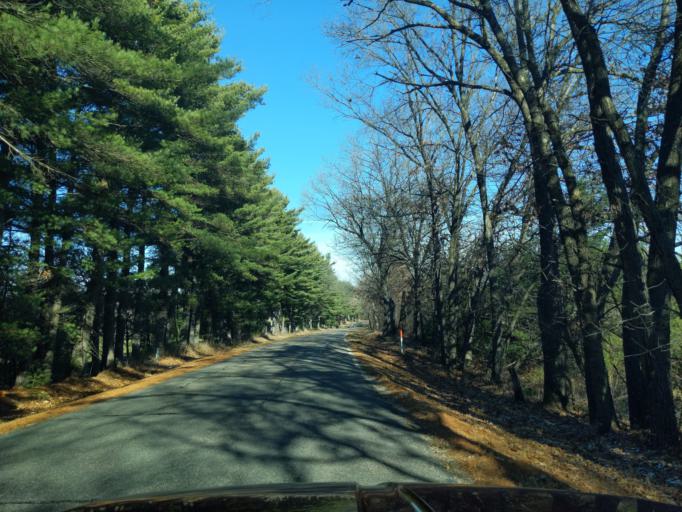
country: US
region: Wisconsin
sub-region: Waushara County
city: Silver Lake
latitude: 44.0764
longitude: -89.1939
